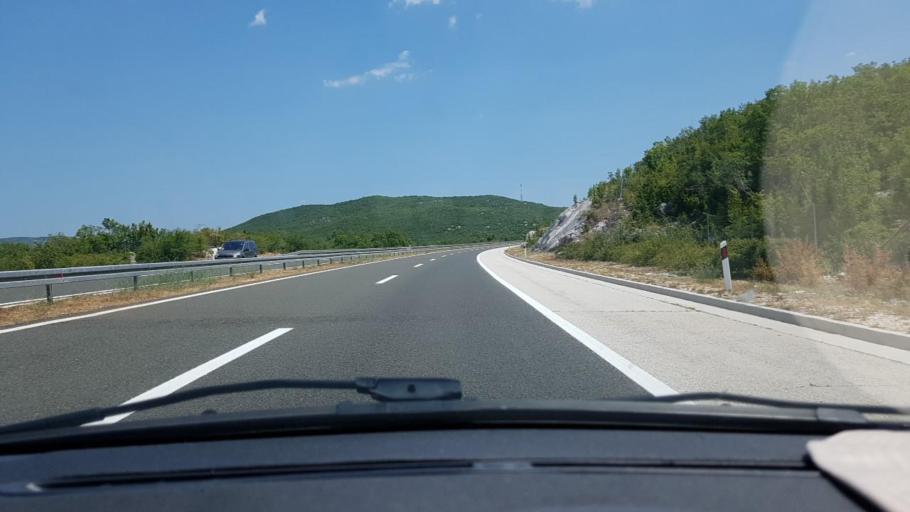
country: HR
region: Splitsko-Dalmatinska
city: Grubine
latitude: 43.3503
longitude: 17.1260
